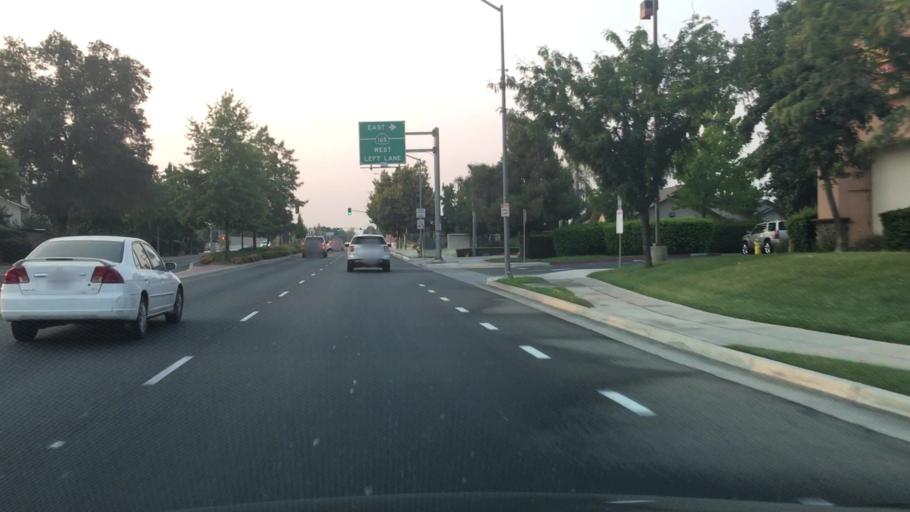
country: US
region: California
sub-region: Fresno County
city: Clovis
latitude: 36.8388
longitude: -119.6839
